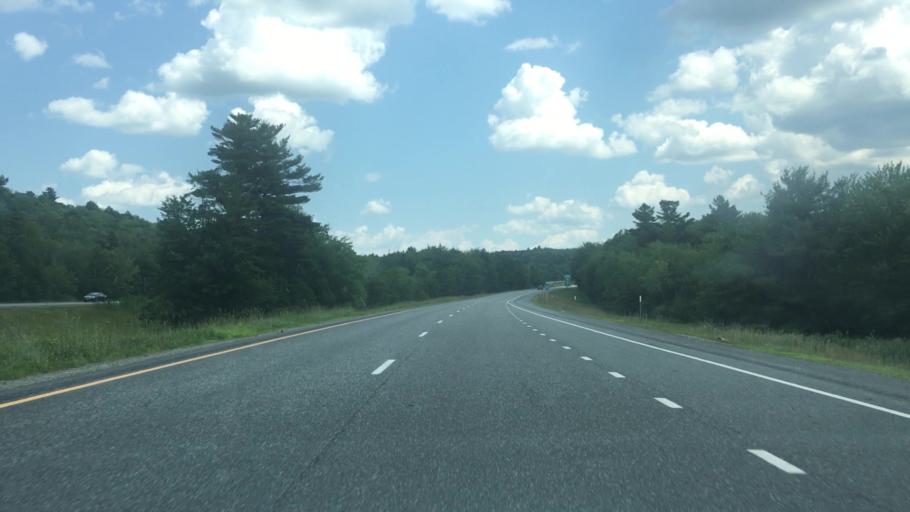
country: US
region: New Hampshire
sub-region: Sullivan County
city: Springfield
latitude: 43.4402
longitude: -72.0572
